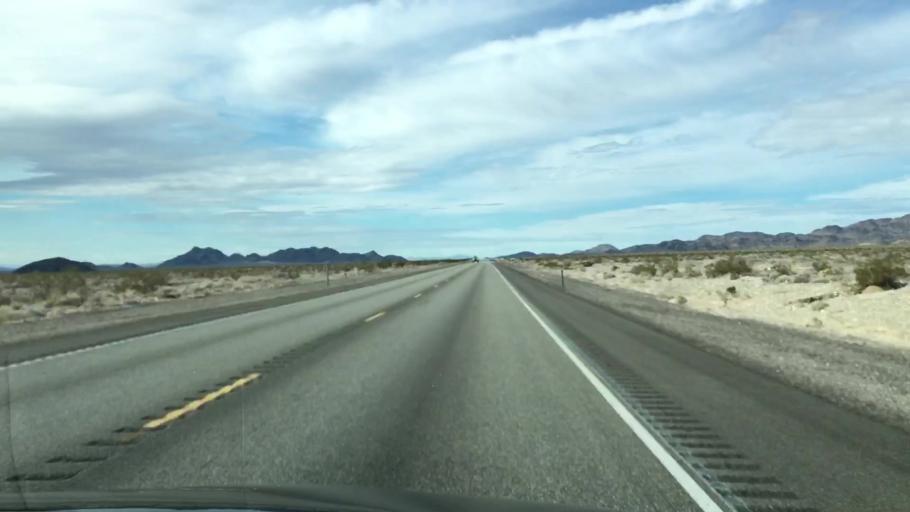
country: US
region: Nevada
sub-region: Nye County
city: Pahrump
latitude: 36.5905
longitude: -116.2245
